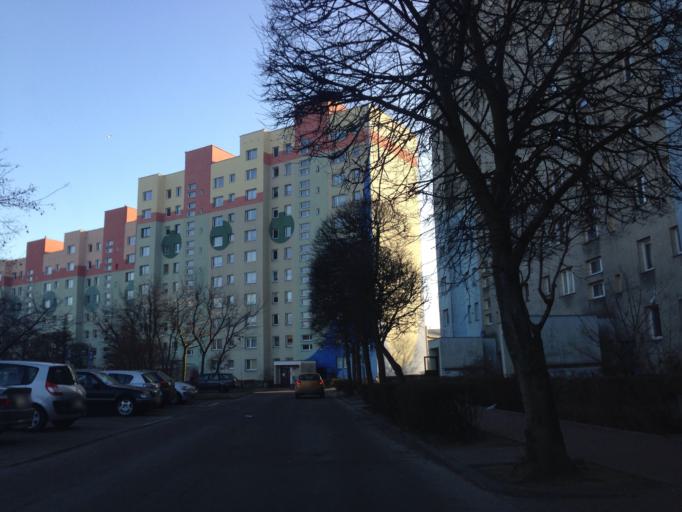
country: PL
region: Pomeranian Voivodeship
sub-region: Gdansk
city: Gdansk
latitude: 54.3922
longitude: 18.6138
